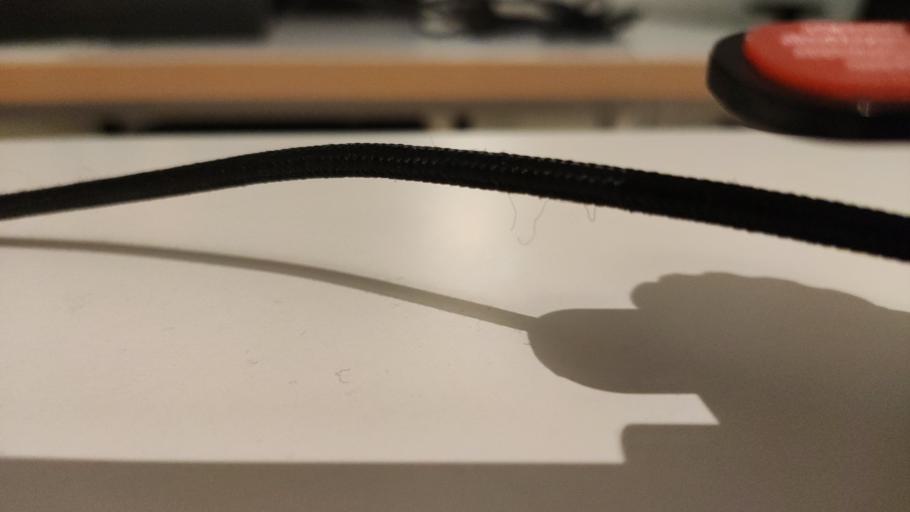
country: RU
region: Moskovskaya
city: Novosin'kovo
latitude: 56.3798
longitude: 37.3252
